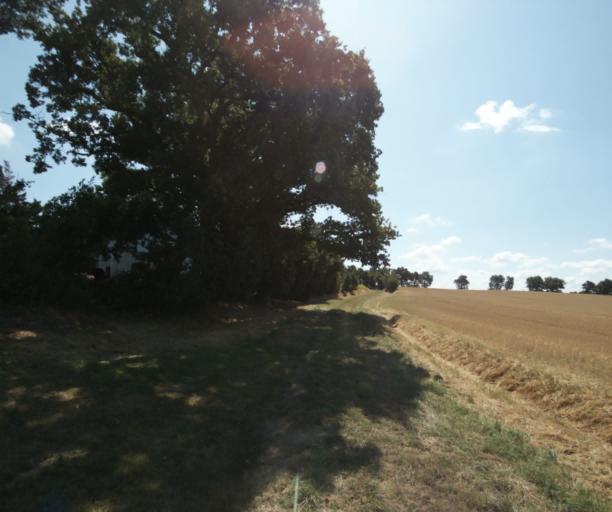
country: FR
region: Midi-Pyrenees
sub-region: Departement de la Haute-Garonne
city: Auriac-sur-Vendinelle
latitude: 43.4636
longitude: 1.8094
